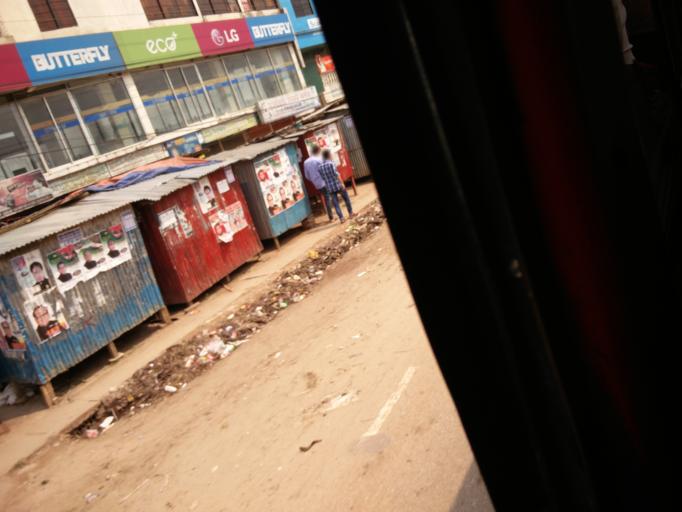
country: BD
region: Dhaka
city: Gafargaon
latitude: 24.2962
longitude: 90.3890
